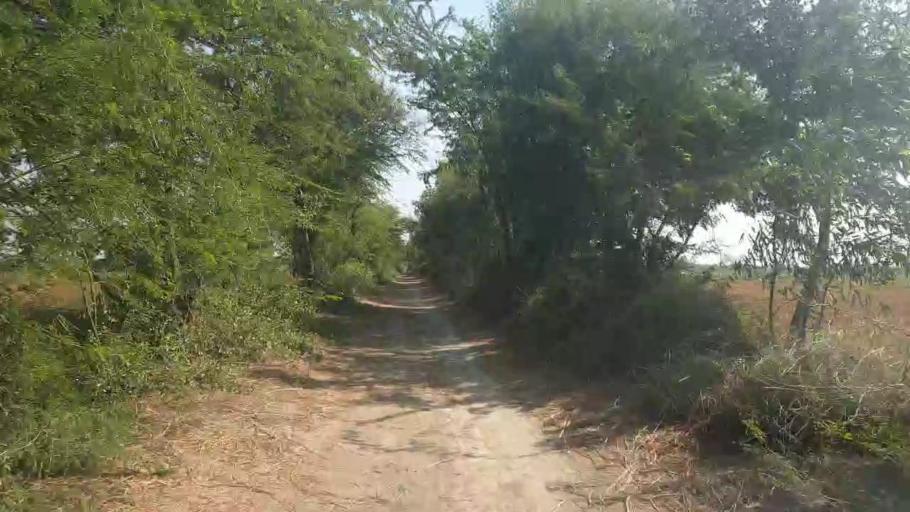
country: PK
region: Sindh
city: Badin
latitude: 24.7123
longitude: 68.8816
